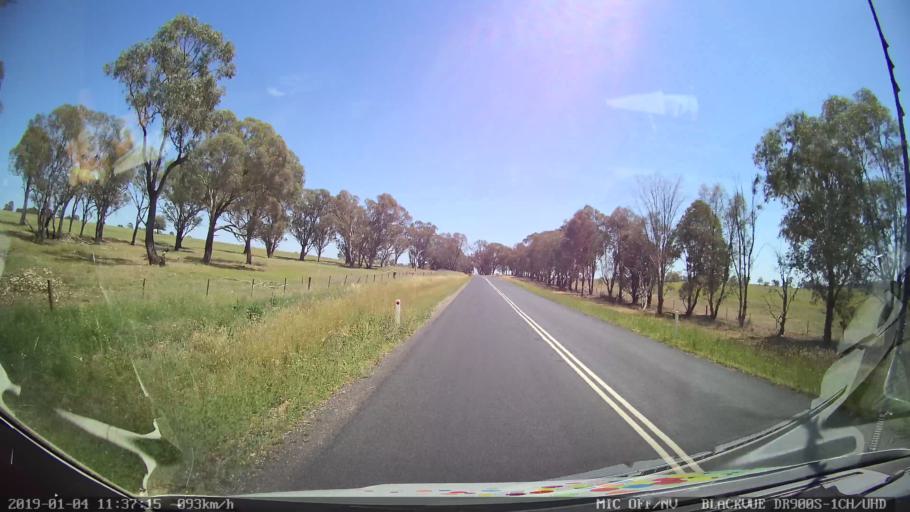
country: AU
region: New South Wales
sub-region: Cabonne
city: Molong
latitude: -33.0347
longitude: 148.8085
